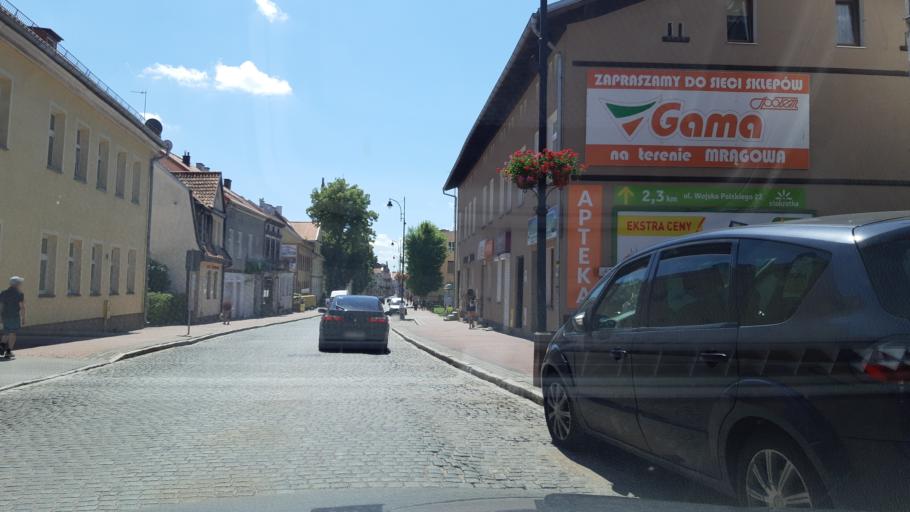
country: PL
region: Warmian-Masurian Voivodeship
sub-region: Powiat mragowski
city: Mragowo
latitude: 53.8753
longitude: 21.3041
